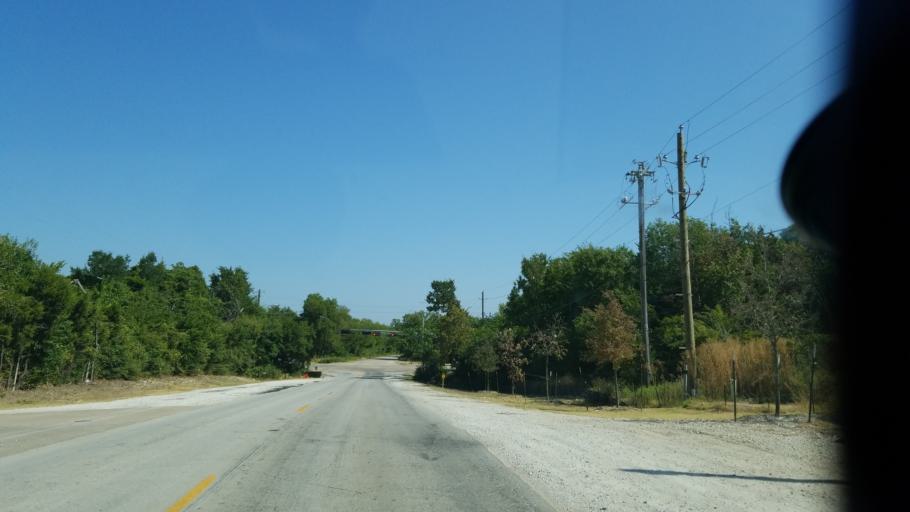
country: US
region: Texas
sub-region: Dallas County
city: Cockrell Hill
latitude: 32.7050
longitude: -96.9257
